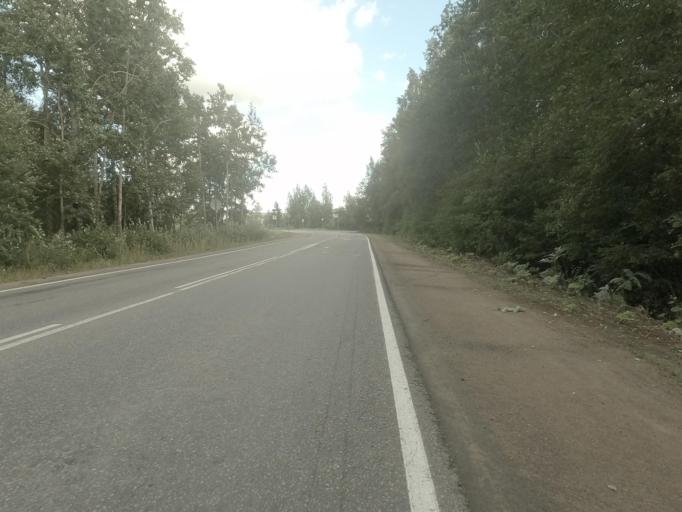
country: RU
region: Leningrad
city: Shcheglovo
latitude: 60.0191
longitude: 30.7427
